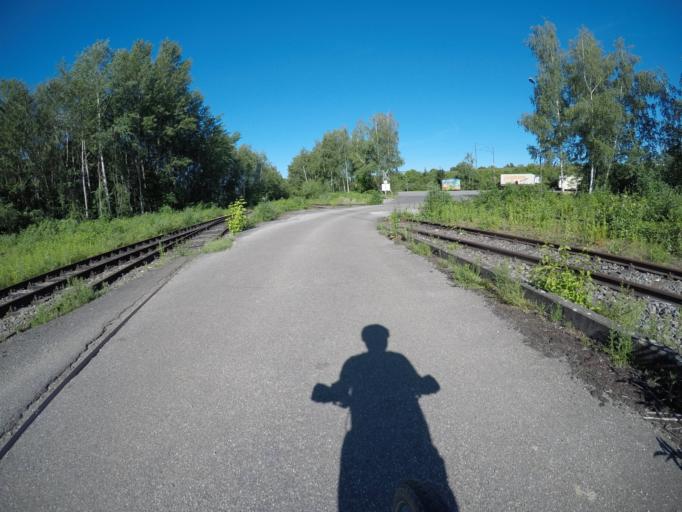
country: DE
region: Baden-Wuerttemberg
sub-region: Karlsruhe Region
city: Karlsruhe
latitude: 49.0021
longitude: 8.4341
